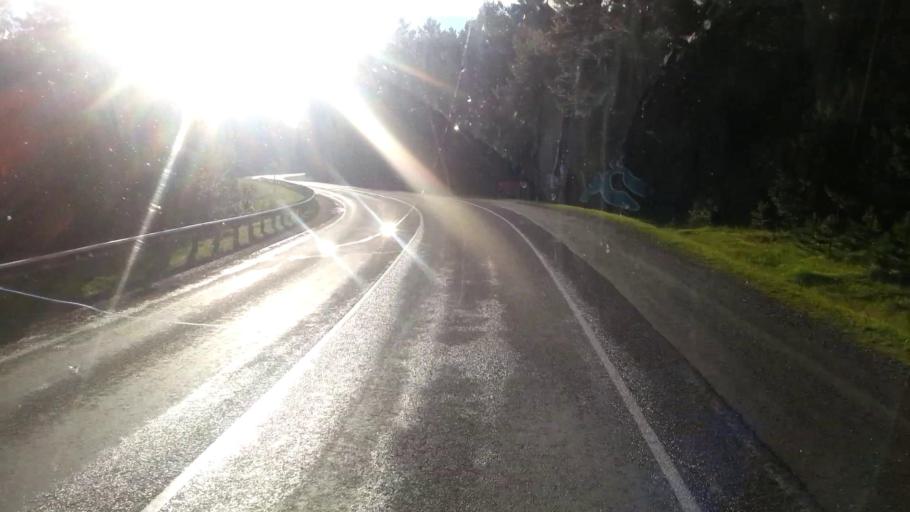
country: RU
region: Altay
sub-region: Mayminskiy Rayon
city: Manzherok
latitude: 51.8319
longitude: 85.7584
